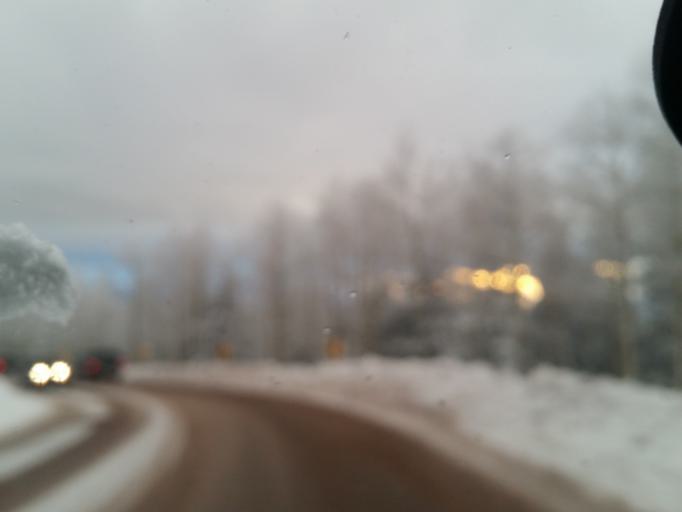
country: US
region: New Mexico
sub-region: Santa Fe County
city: Santa Fe
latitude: 35.7793
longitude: -105.8095
